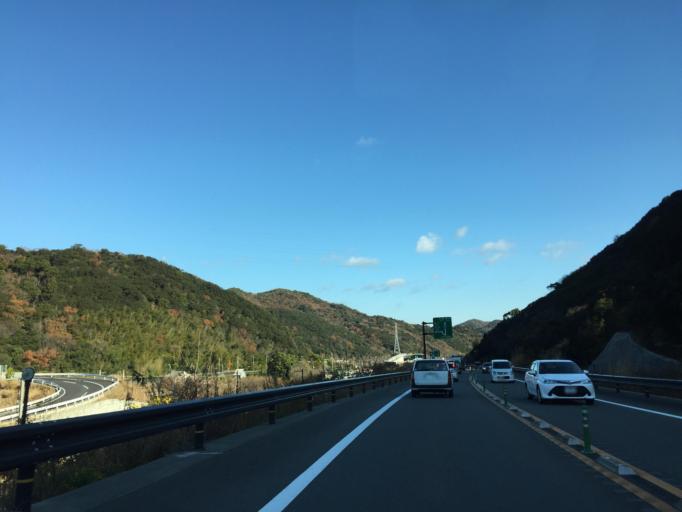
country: JP
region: Wakayama
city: Wakayama-shi
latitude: 34.2931
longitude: 135.1515
